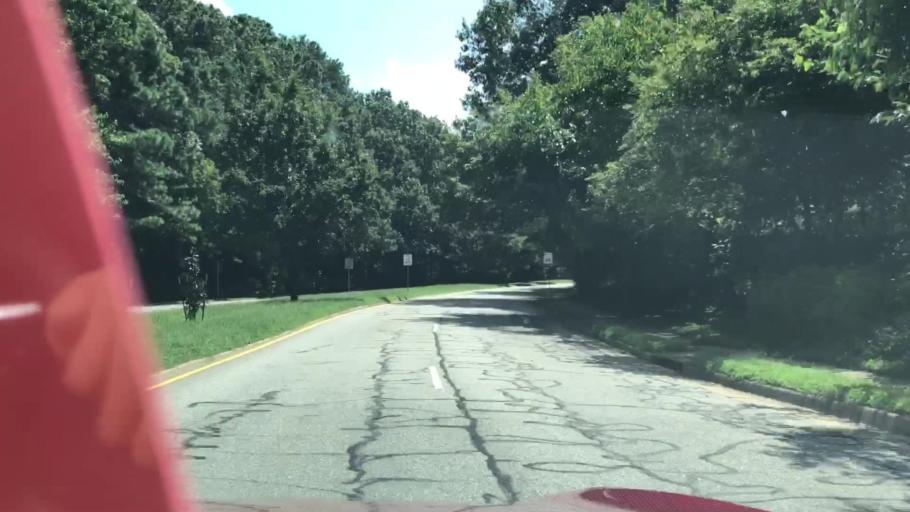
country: US
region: Virginia
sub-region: City of Virginia Beach
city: Virginia Beach
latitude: 36.8737
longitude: -76.0374
